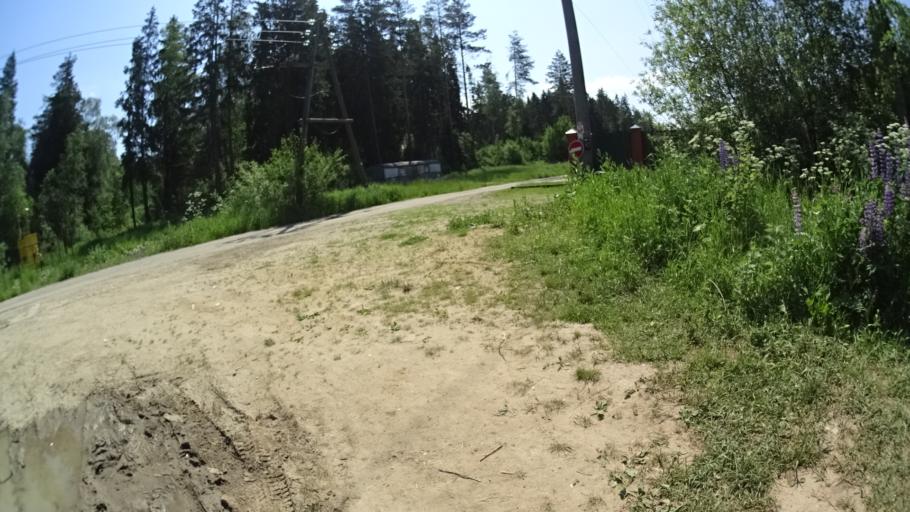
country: RU
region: Moskovskaya
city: Zelenogradskiy
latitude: 56.0845
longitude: 37.9585
